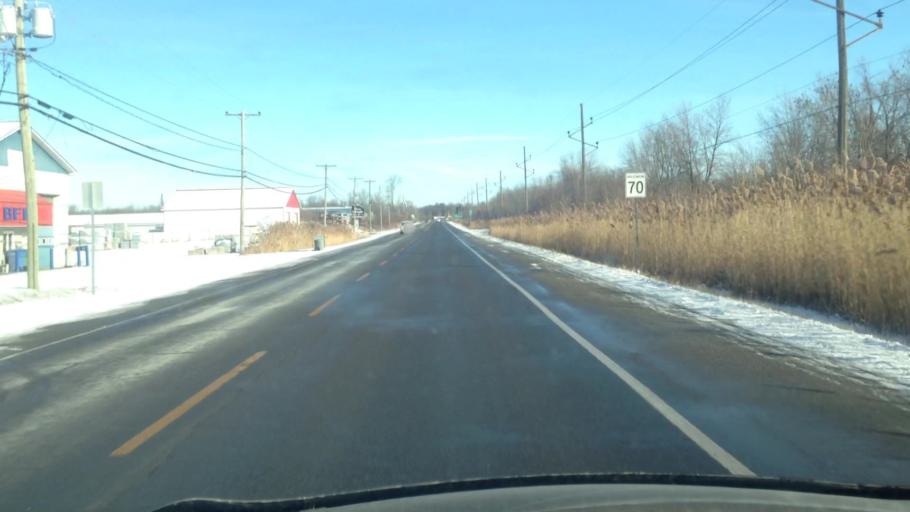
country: CA
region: Quebec
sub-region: Monteregie
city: Beauharnois
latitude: 45.3224
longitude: -73.8327
